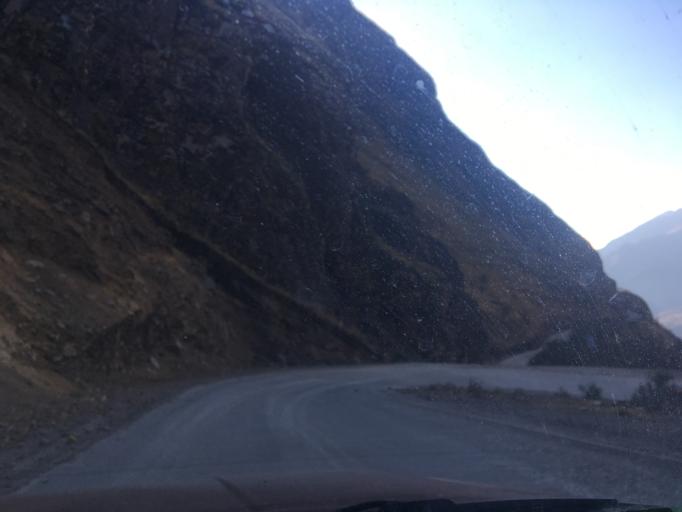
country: BO
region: La Paz
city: Quime
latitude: -17.0003
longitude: -67.2811
